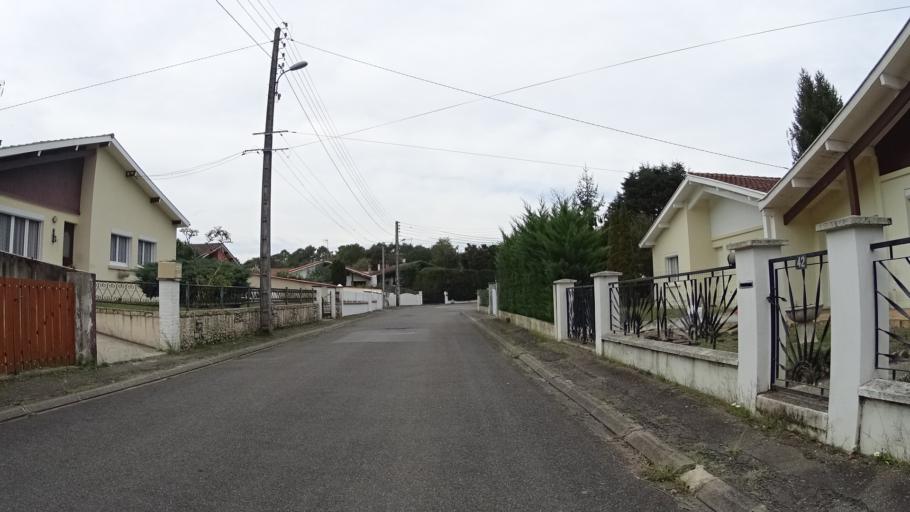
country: FR
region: Aquitaine
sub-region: Departement des Landes
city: Saint-Paul-les-Dax
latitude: 43.7306
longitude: -1.0774
